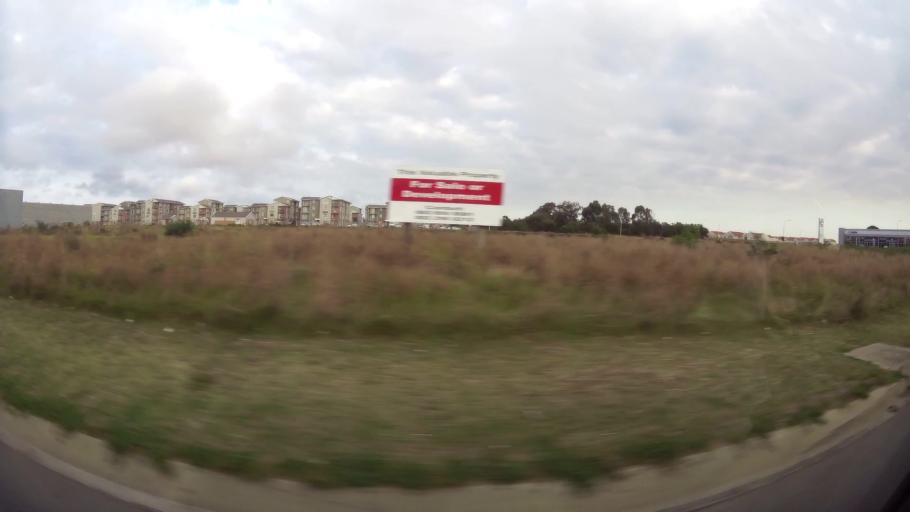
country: ZA
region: Eastern Cape
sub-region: Nelson Mandela Bay Metropolitan Municipality
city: Port Elizabeth
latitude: -33.9705
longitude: 25.5546
